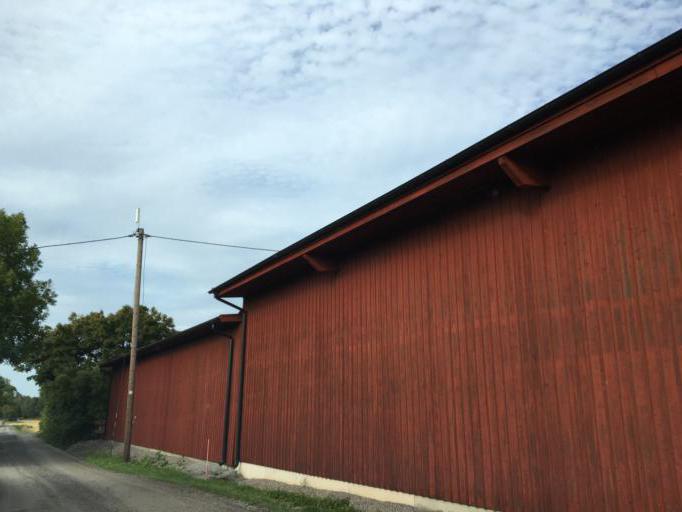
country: SE
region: Soedermanland
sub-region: Eskilstuna Kommun
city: Eskilstuna
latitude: 59.4082
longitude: 16.5122
